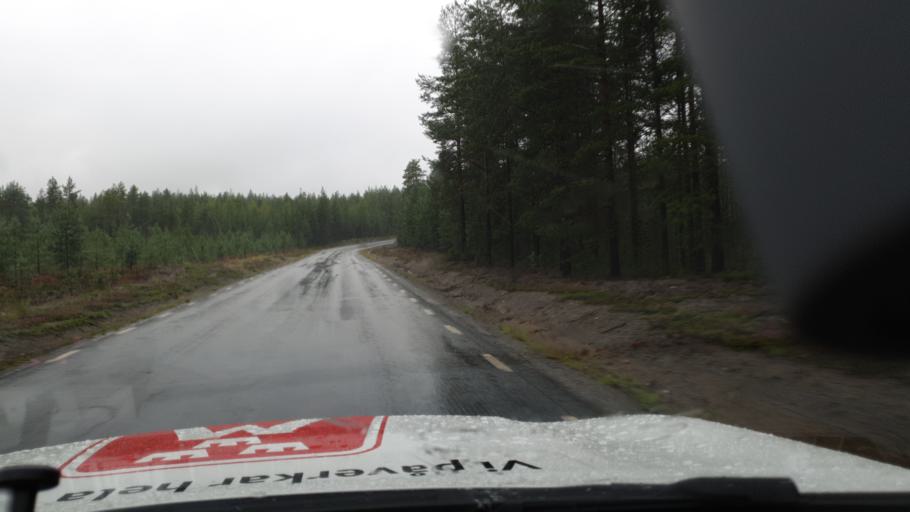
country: SE
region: Vaesterbotten
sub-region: Skelleftea Kommun
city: Burea
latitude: 64.6081
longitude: 21.1554
